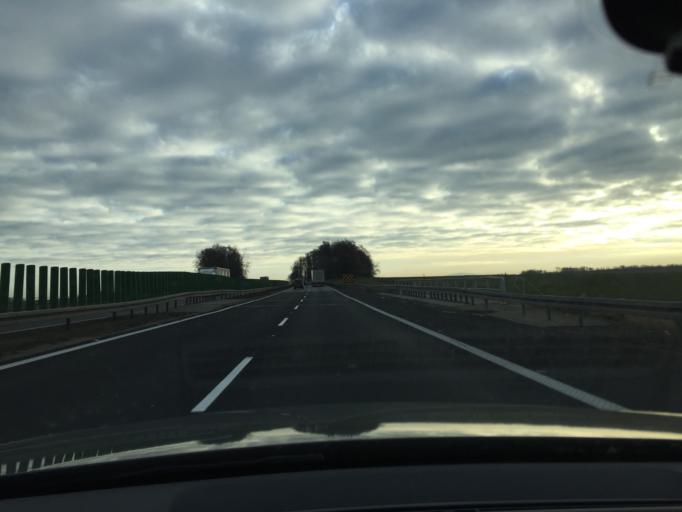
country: PL
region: Lower Silesian Voivodeship
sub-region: Powiat legnicki
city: Legnickie Pole
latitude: 51.1327
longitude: 16.3010
